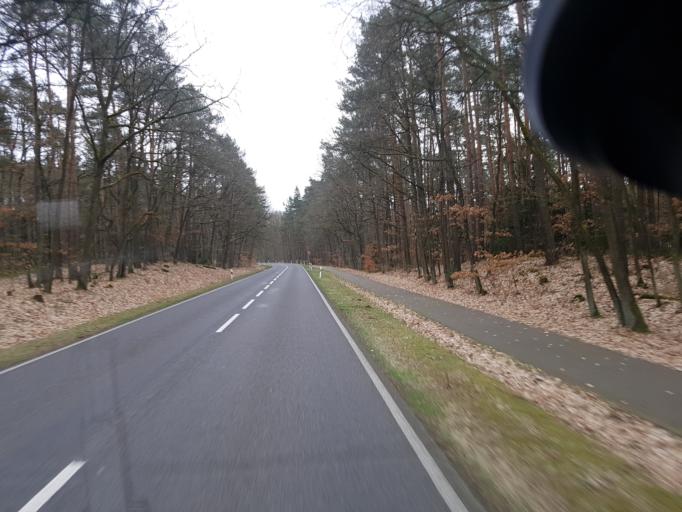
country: DE
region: Brandenburg
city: Gross Lindow
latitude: 52.1760
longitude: 14.4811
